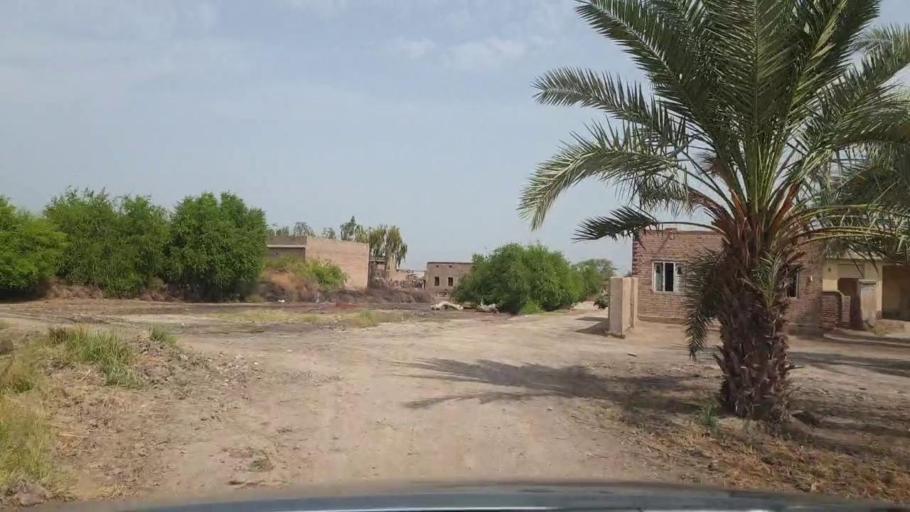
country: PK
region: Sindh
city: Rohri
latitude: 27.6886
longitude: 69.0372
